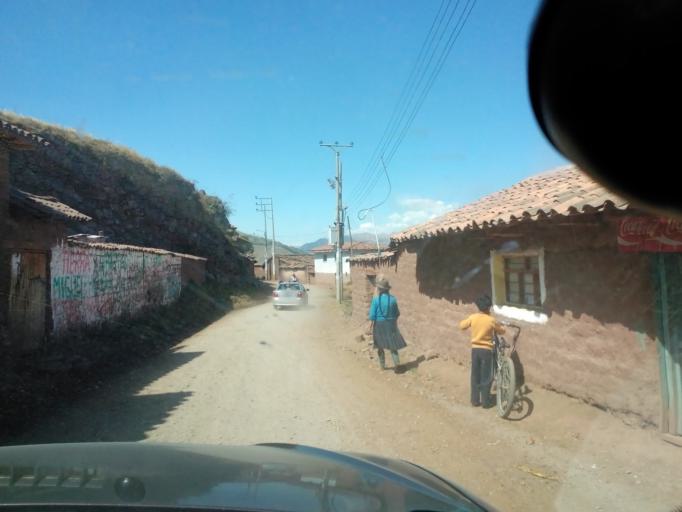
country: PE
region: Cusco
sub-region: Provincia de Anta
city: Zurite
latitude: -13.4370
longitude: -72.2297
